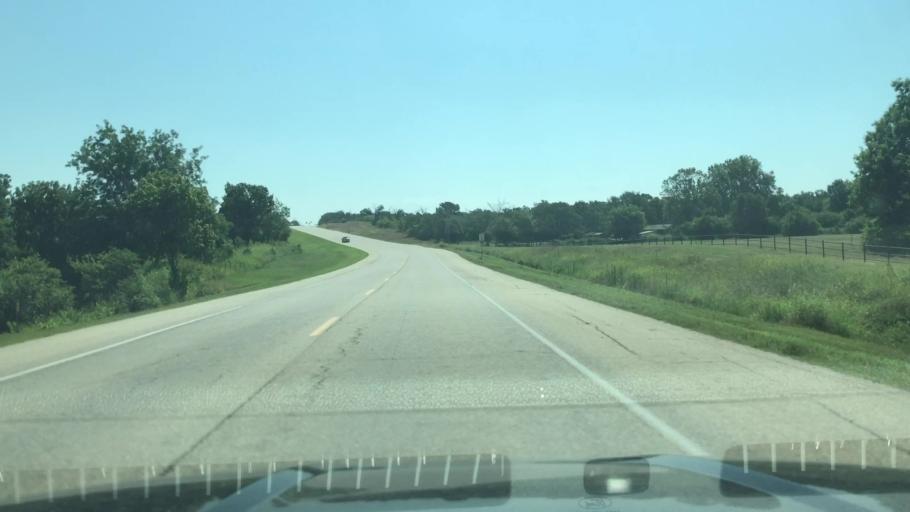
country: US
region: Oklahoma
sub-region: Creek County
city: Mannford
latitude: 36.0028
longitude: -96.3973
